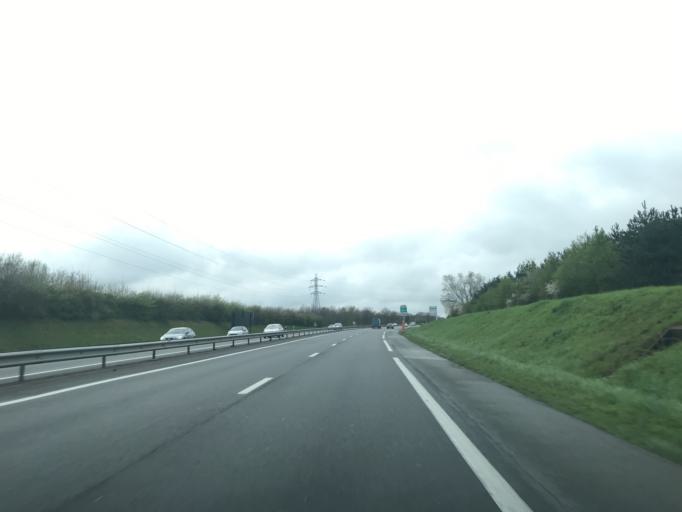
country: FR
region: Centre
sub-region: Departement du Loiret
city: Boigny-sur-Bionne
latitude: 47.9204
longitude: 2.0002
